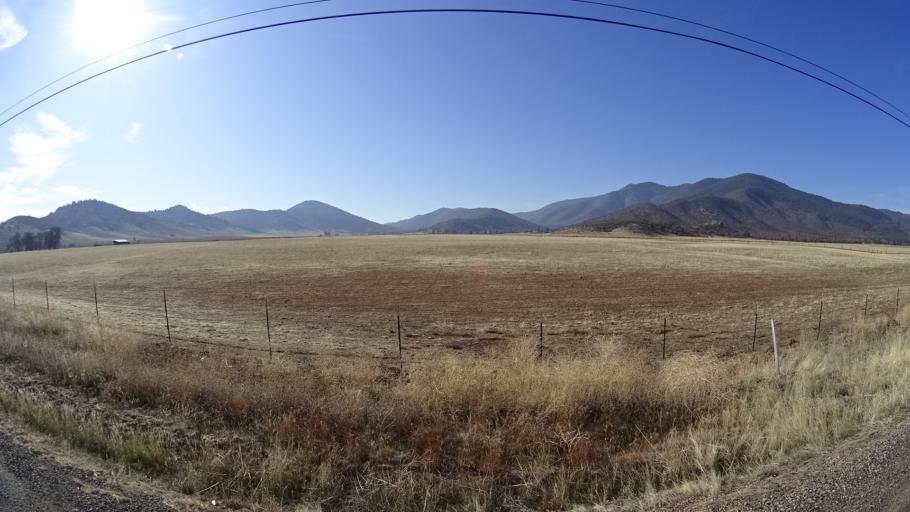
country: US
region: California
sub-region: Siskiyou County
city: Montague
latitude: 41.6535
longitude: -122.5615
